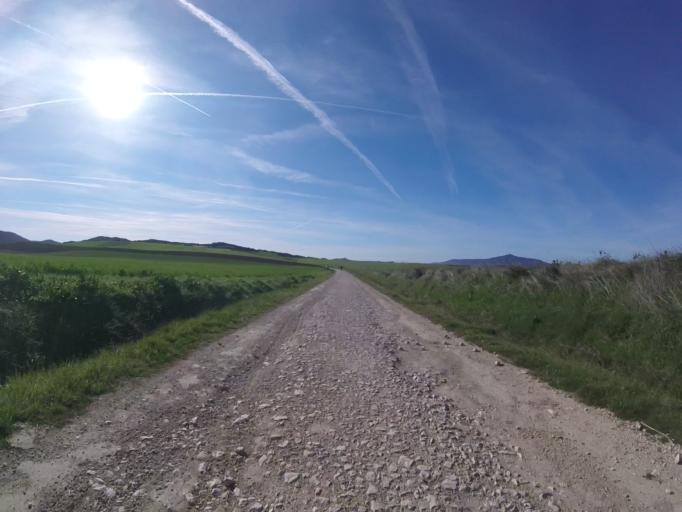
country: ES
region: Navarre
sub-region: Provincia de Navarra
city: Yerri
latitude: 42.7144
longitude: -1.9705
